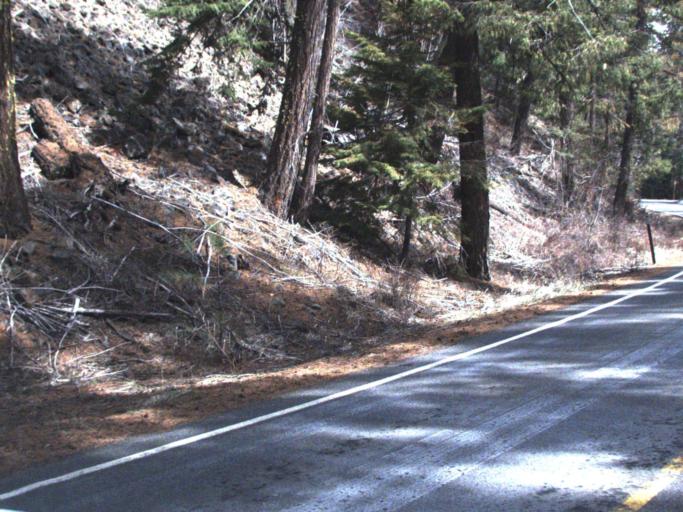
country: US
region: Washington
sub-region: Kittitas County
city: Cle Elum
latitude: 46.9864
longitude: -121.1112
